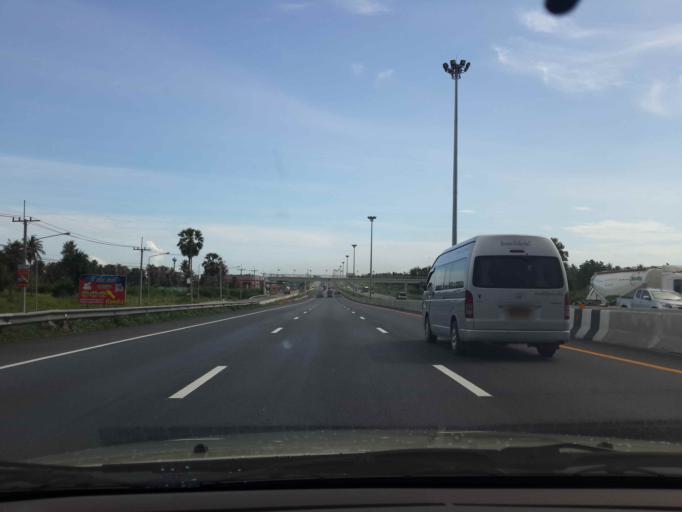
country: TH
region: Chon Buri
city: Ban Talat Bueng
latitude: 13.0186
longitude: 100.9963
